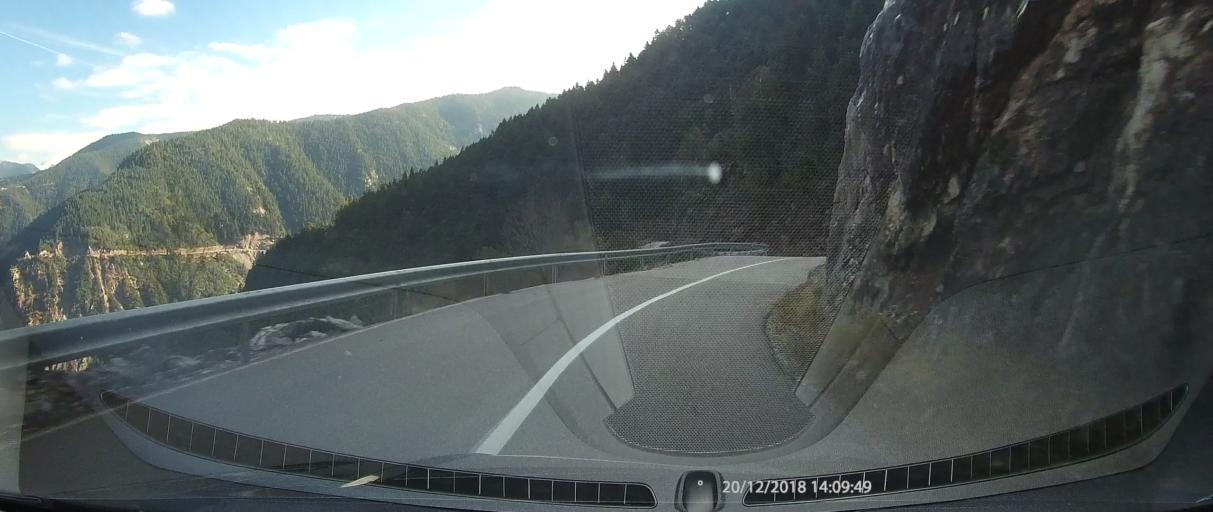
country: GR
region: West Greece
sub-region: Nomos Aitolias kai Akarnanias
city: Thermo
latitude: 38.7493
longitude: 21.6452
